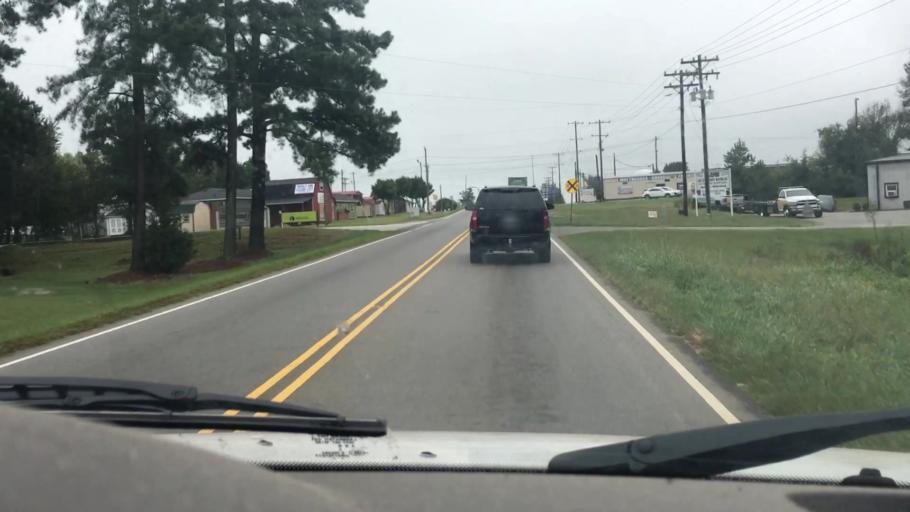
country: US
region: North Carolina
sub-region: Iredell County
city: Mooresville
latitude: 35.6023
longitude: -80.8102
